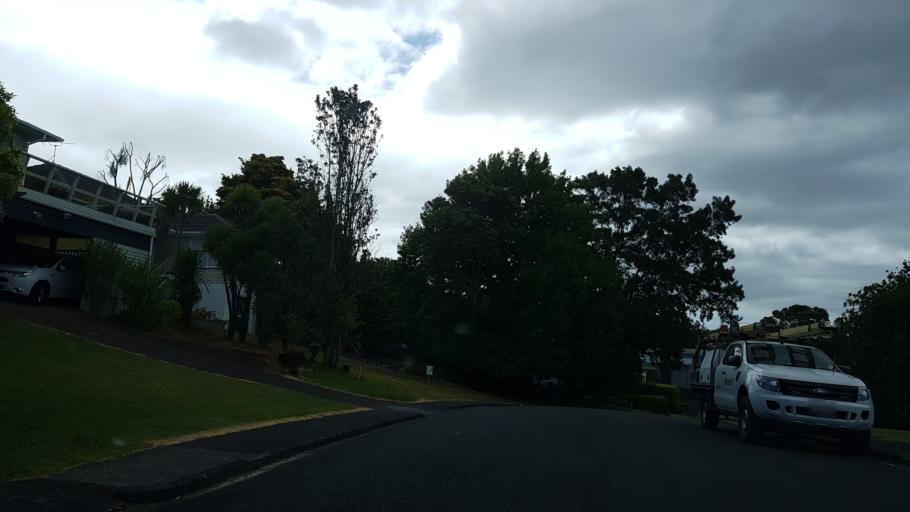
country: NZ
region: Auckland
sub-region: Auckland
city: North Shore
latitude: -36.7783
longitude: 174.7292
